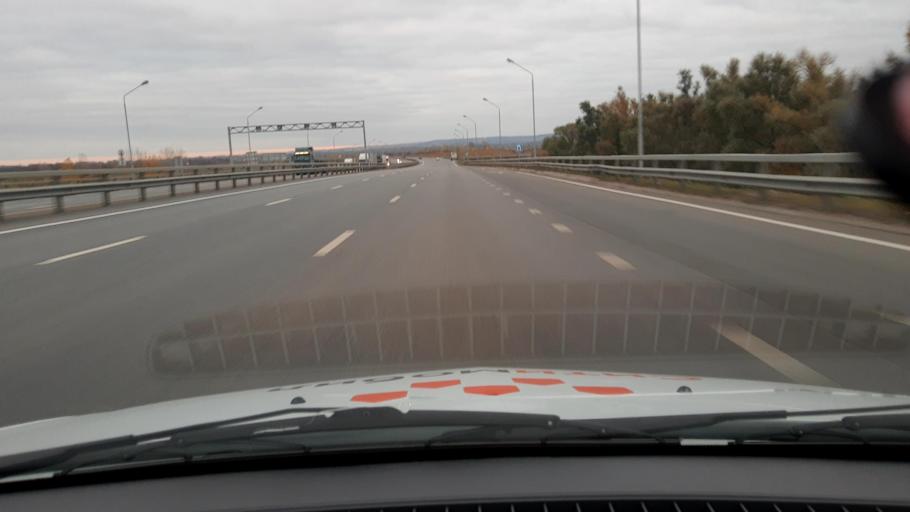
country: RU
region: Bashkortostan
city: Ufa
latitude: 54.6435
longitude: 55.9383
